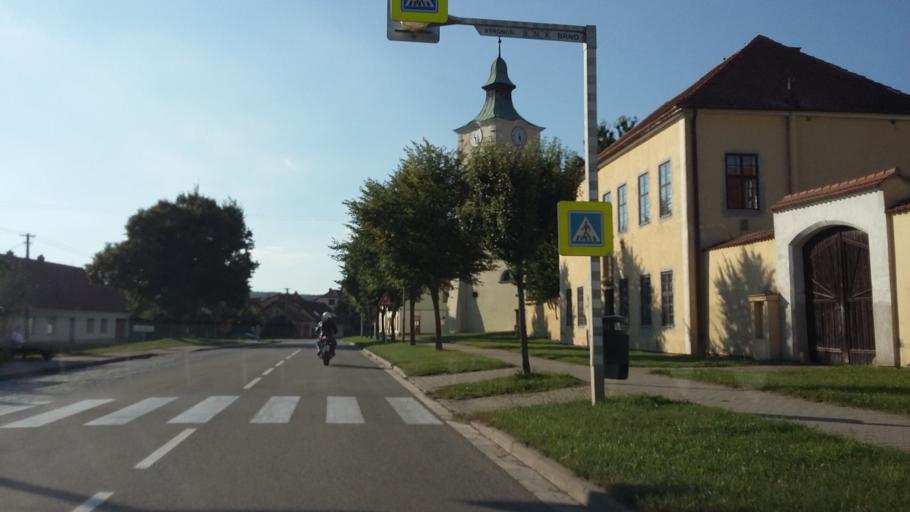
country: CZ
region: South Moravian
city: Ricany
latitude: 49.2107
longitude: 16.4095
